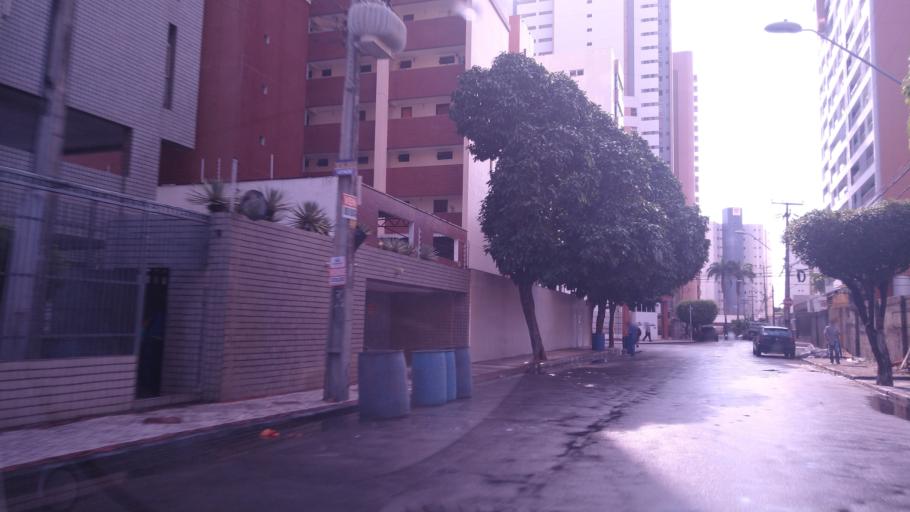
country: BR
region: Ceara
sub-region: Fortaleza
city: Fortaleza
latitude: -3.7275
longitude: -38.4907
